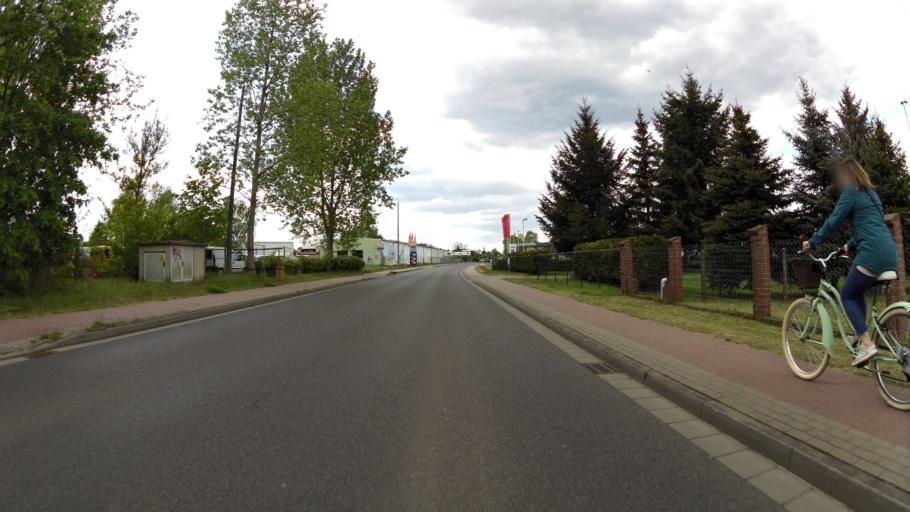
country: DE
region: Brandenburg
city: Furstenwalde
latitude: 52.3782
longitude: 14.0715
